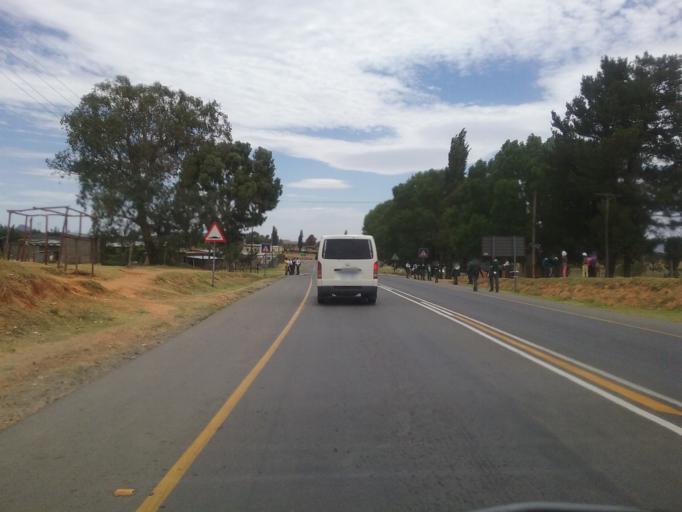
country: LS
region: Maseru
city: Maseru
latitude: -29.4872
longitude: 27.5269
